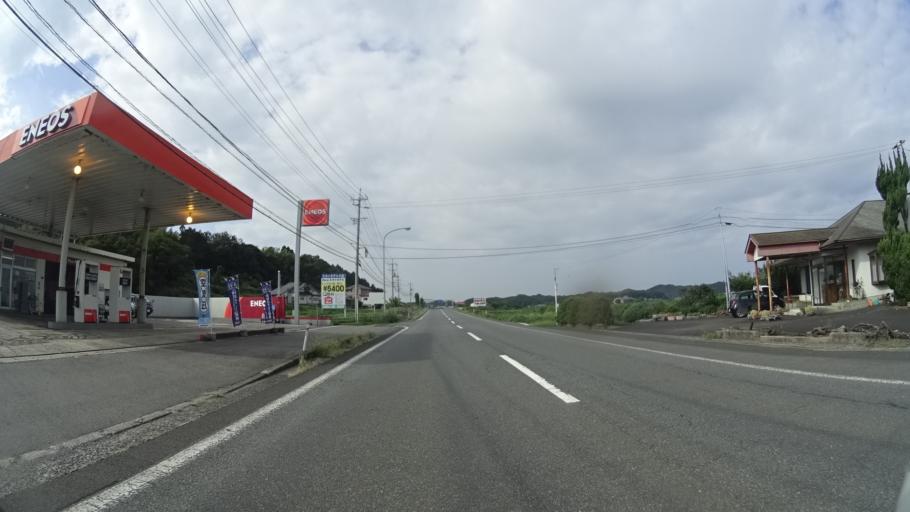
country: JP
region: Shimane
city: Odacho-oda
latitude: 35.2272
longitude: 132.5199
